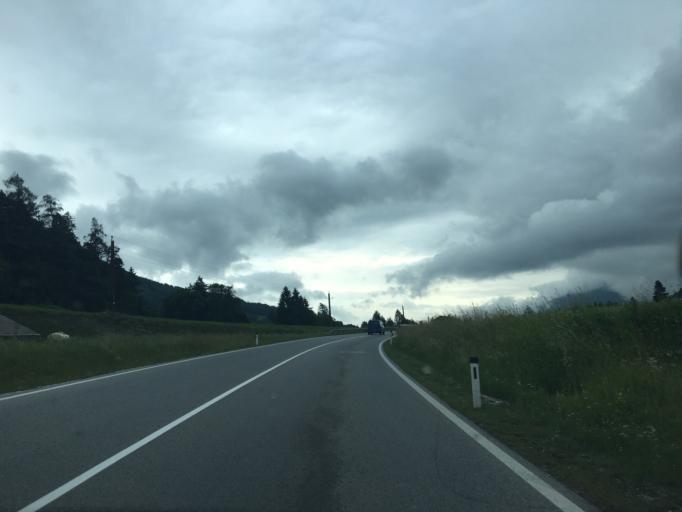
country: AT
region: Tyrol
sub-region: Politischer Bezirk Innsbruck Land
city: Telfes im Stubai
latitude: 47.1655
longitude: 11.3732
